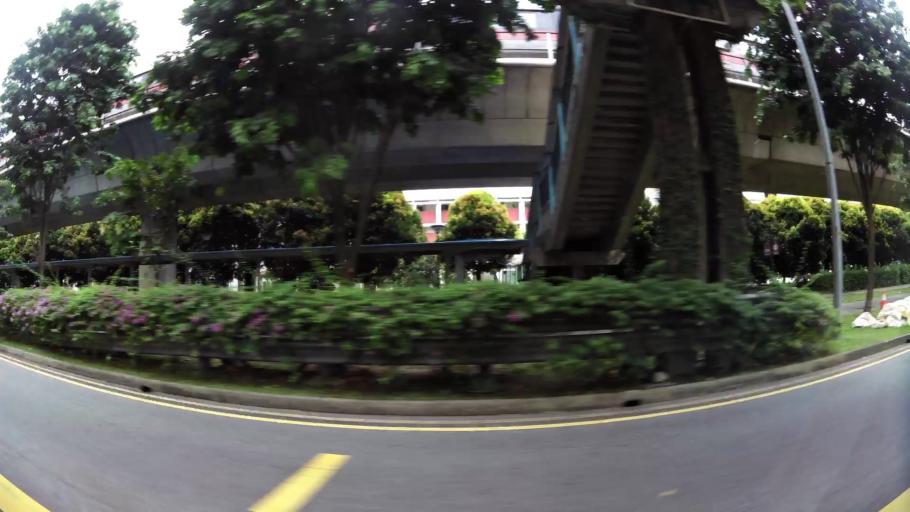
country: MY
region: Johor
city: Kampung Pasir Gudang Baru
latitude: 1.4204
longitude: 103.8347
